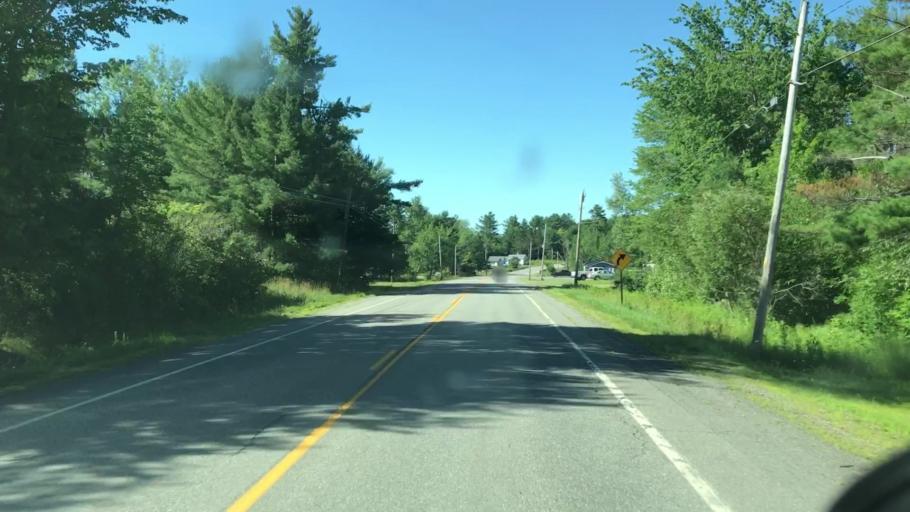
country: US
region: Maine
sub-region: Penobscot County
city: Howland
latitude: 45.2898
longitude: -68.6233
